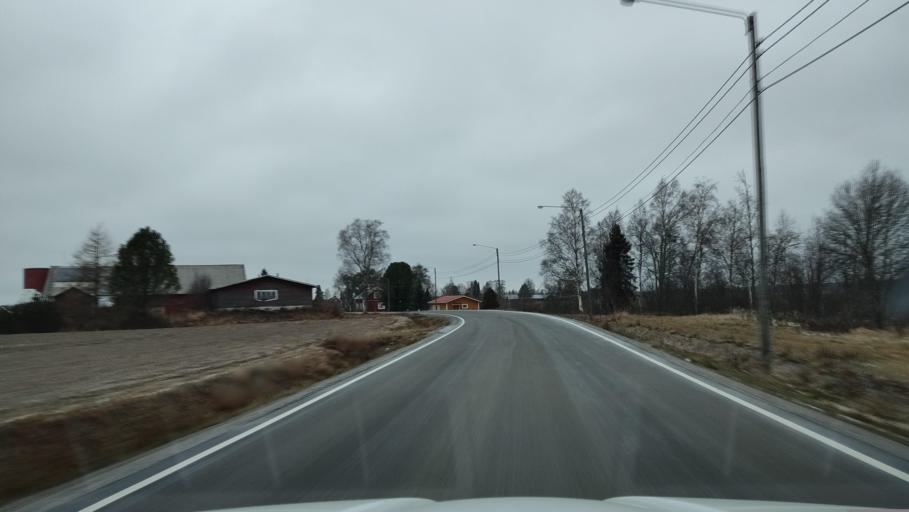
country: FI
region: Southern Ostrobothnia
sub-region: Suupohja
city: Karijoki
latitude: 62.2427
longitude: 21.5621
